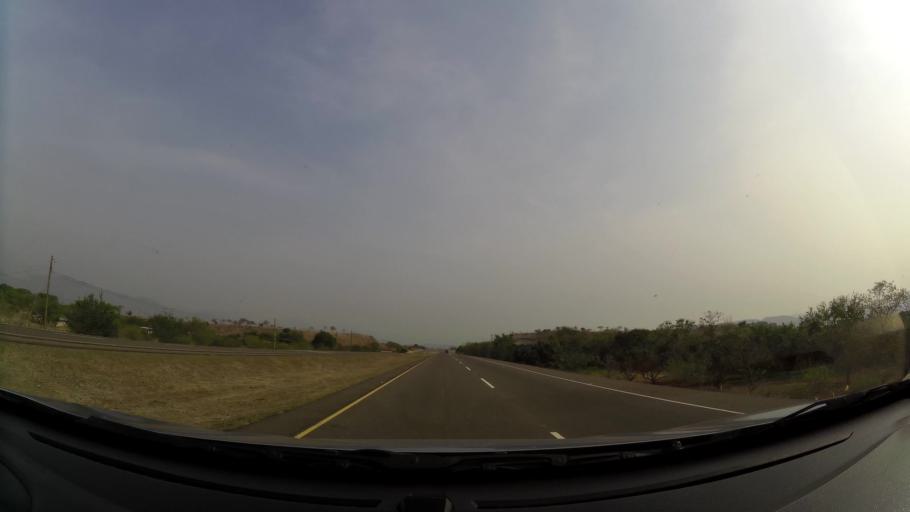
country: HN
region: Comayagua
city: Comayagua
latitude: 14.4458
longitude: -87.6613
